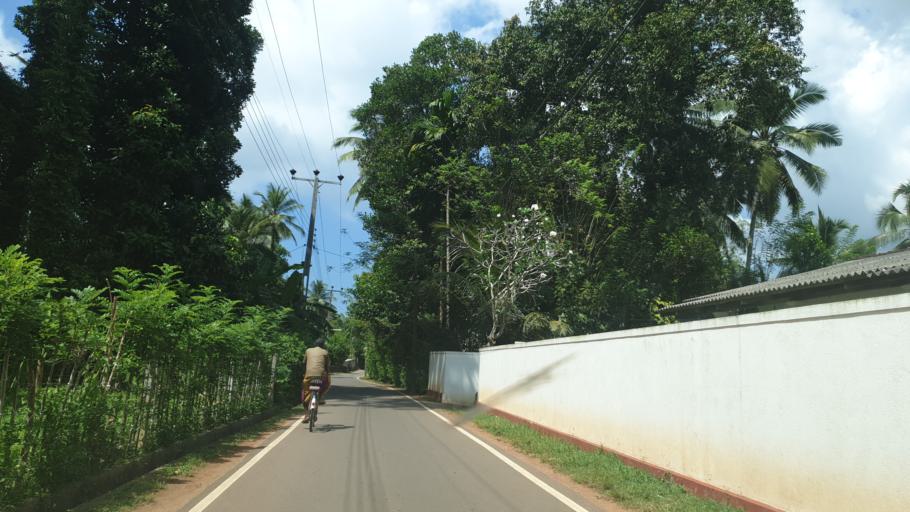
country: LK
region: Western
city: Panadura
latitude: 6.6755
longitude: 79.9726
